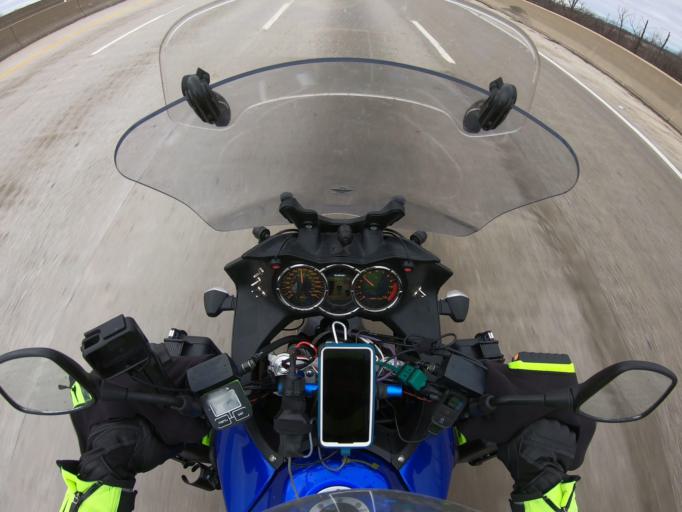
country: US
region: Michigan
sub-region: Saginaw County
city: Zilwaukee
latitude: 43.4782
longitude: -83.9033
